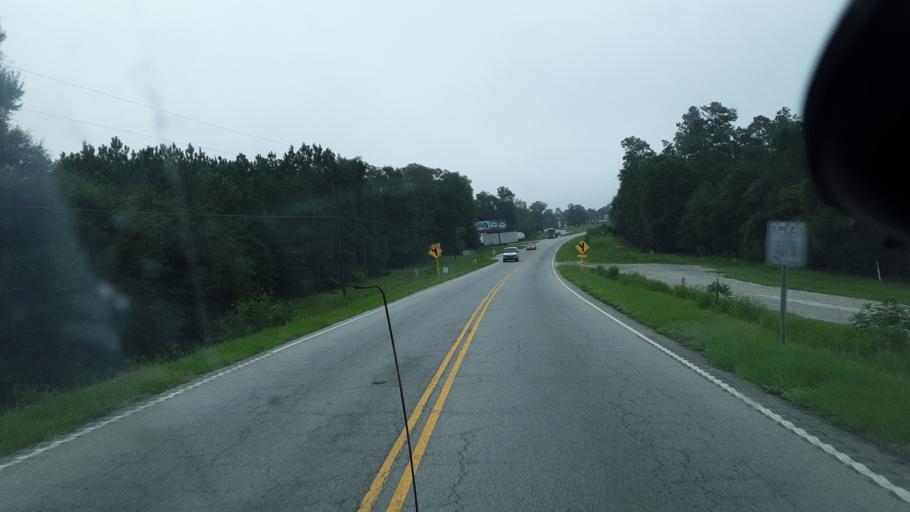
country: US
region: South Carolina
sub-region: Florence County
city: Johnsonville
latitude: 33.9141
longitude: -79.4120
